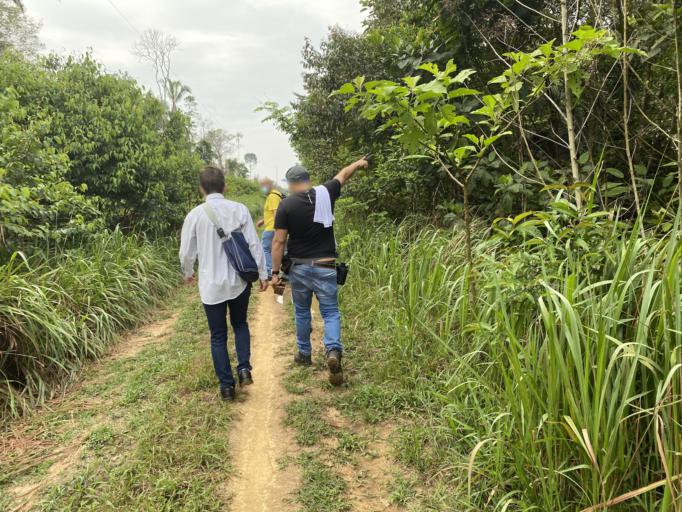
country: BR
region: Rondonia
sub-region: Porto Velho
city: Porto Velho
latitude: -8.8361
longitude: -64.2316
